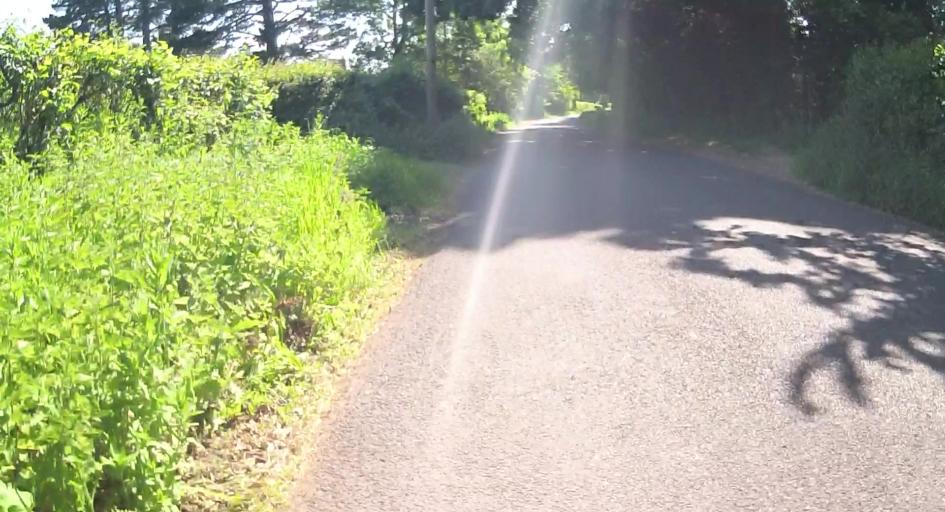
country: GB
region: England
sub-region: Hampshire
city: Kingsclere
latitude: 51.3379
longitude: -1.2801
